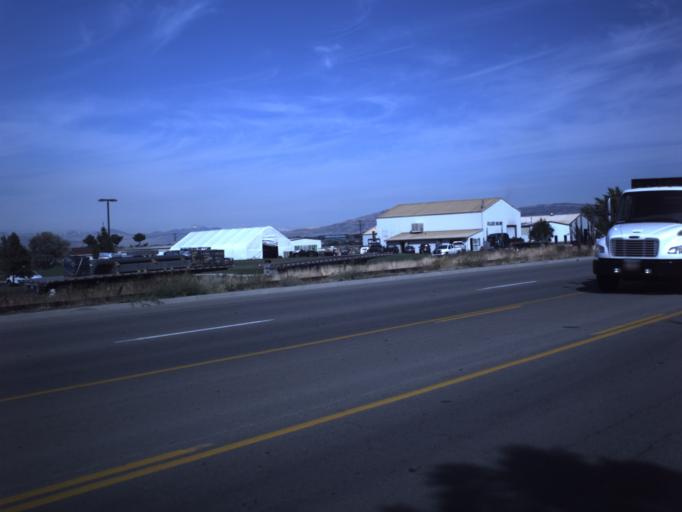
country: US
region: Utah
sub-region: Utah County
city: Pleasant Grove
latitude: 40.3448
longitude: -111.7406
